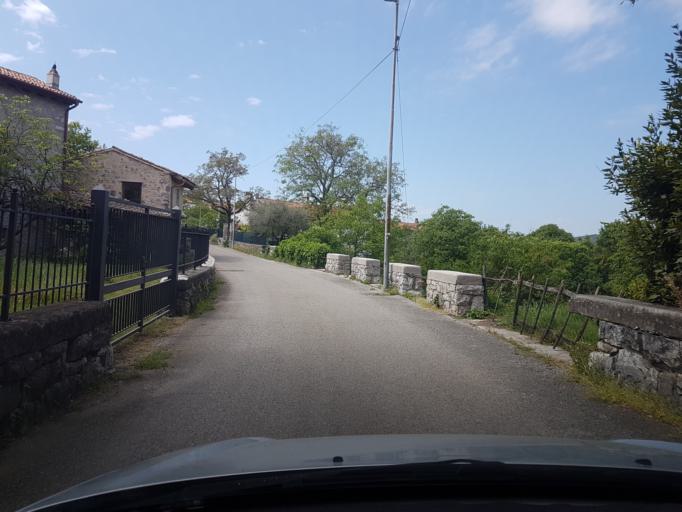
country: IT
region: Friuli Venezia Giulia
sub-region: Provincia di Trieste
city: Sistiana-Visogliano
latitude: 45.7859
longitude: 13.6587
